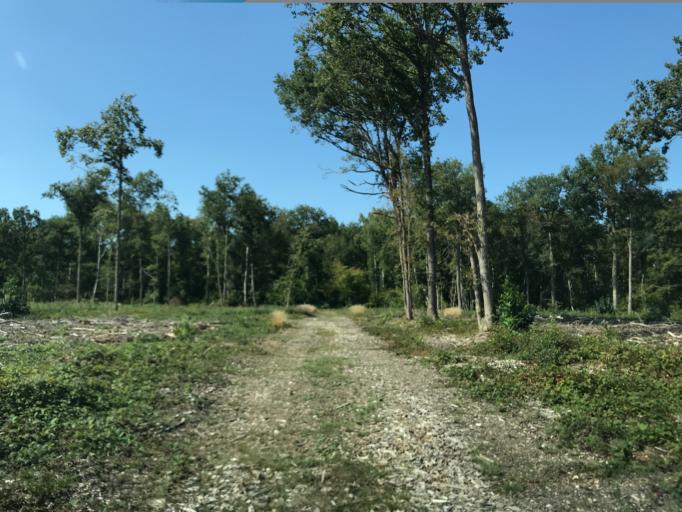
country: FR
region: Haute-Normandie
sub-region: Departement de l'Eure
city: Heudreville-sur-Eure
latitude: 49.1077
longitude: 1.2050
